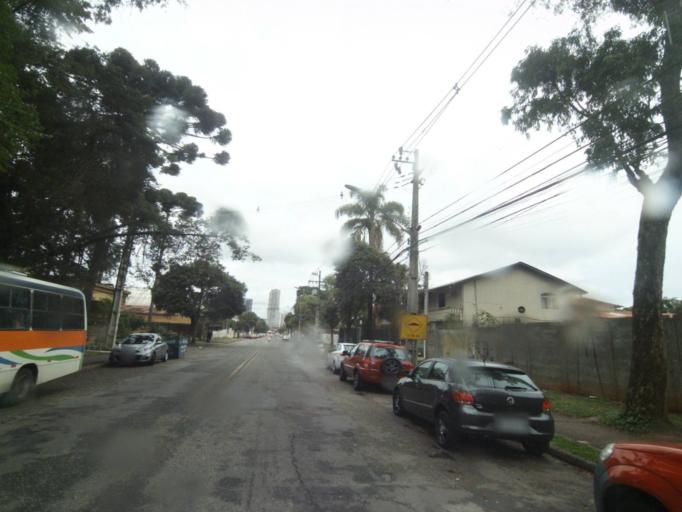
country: BR
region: Parana
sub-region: Curitiba
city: Curitiba
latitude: -25.4462
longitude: -49.3477
